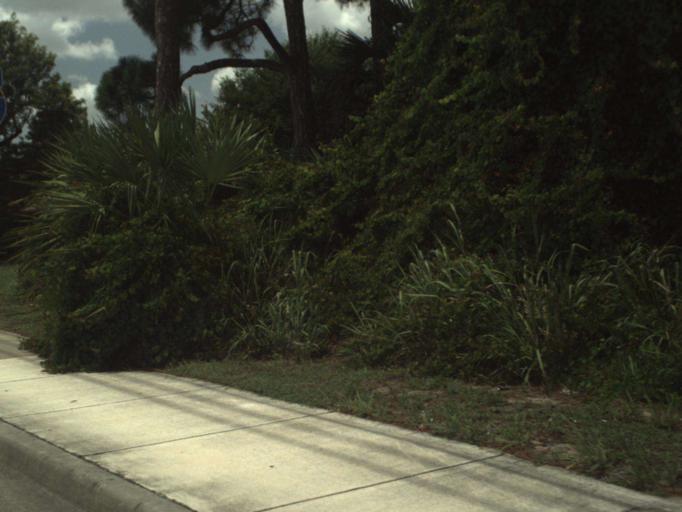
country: US
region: Florida
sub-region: Martin County
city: North River Shores
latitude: 27.2712
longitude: -80.2932
